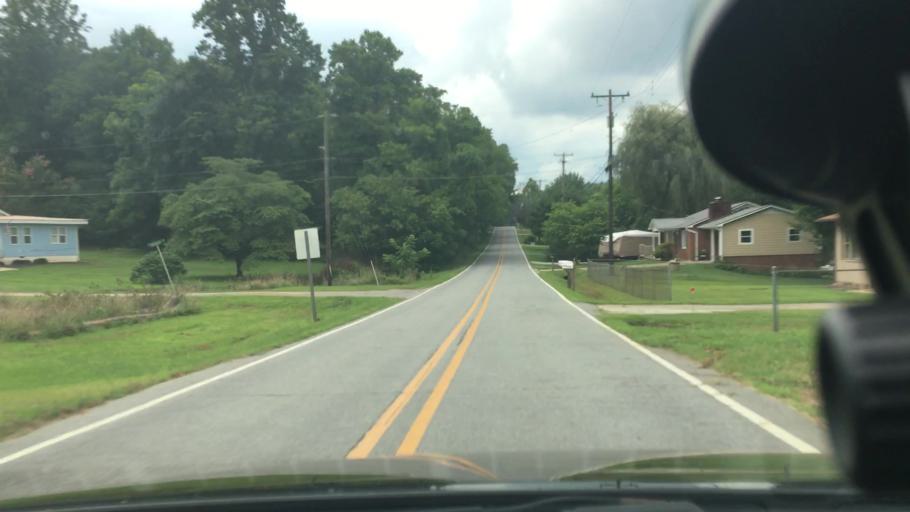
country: US
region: North Carolina
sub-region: McDowell County
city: West Marion
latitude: 35.6607
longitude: -82.0170
